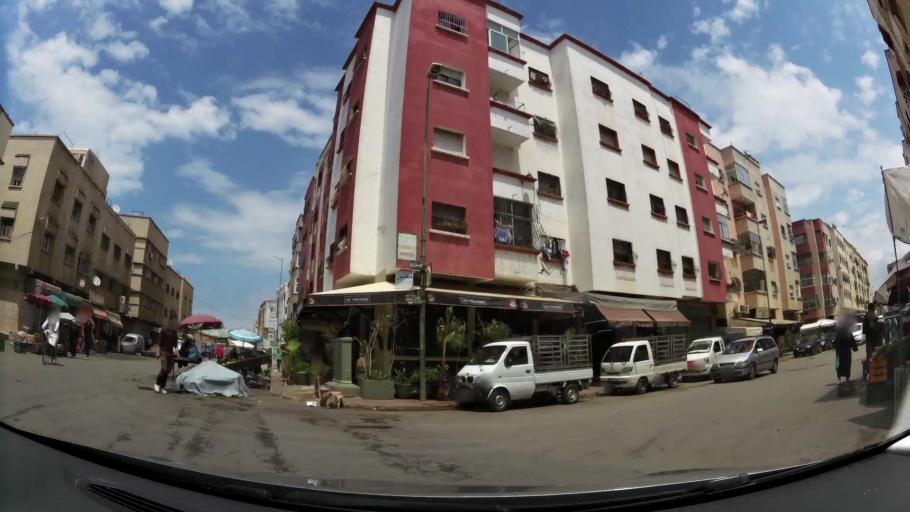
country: MA
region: Rabat-Sale-Zemmour-Zaer
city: Sale
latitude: 34.0498
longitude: -6.8168
